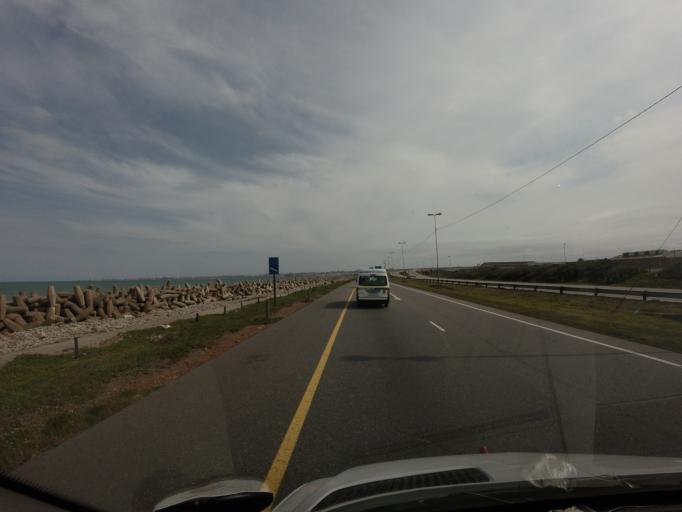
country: ZA
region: Eastern Cape
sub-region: Nelson Mandela Bay Metropolitan Municipality
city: Port Elizabeth
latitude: -33.9091
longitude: 25.6169
